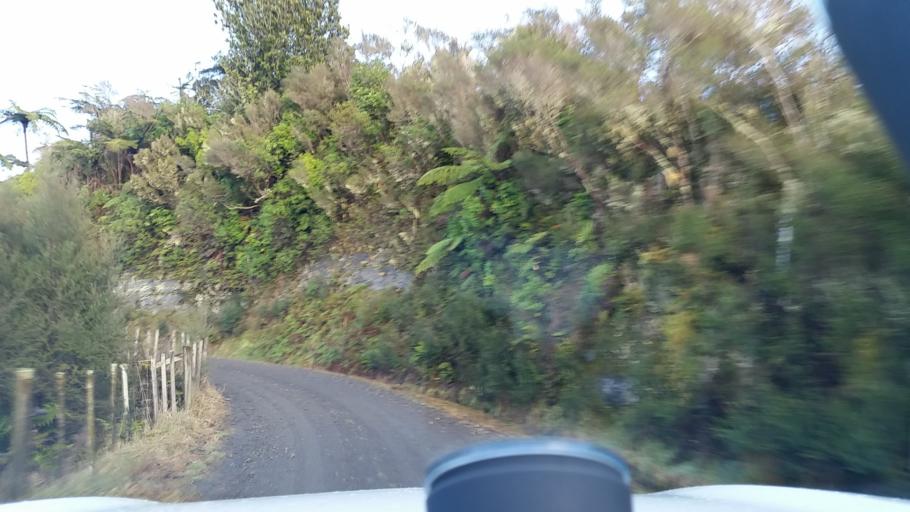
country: NZ
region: Taranaki
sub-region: South Taranaki District
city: Eltham
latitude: -39.4184
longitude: 174.5566
